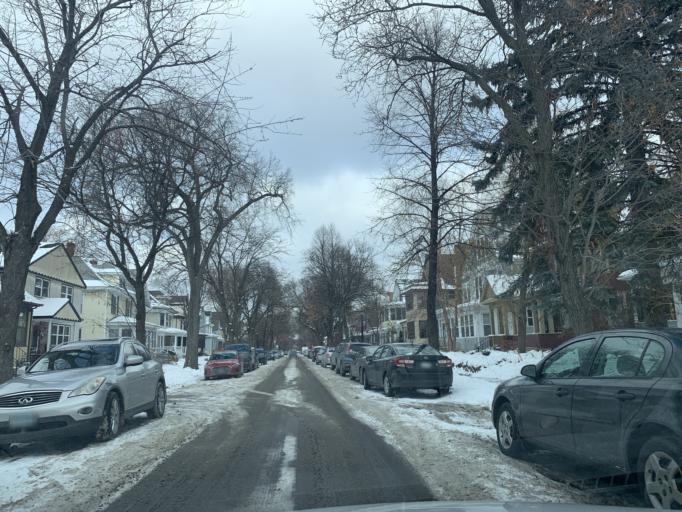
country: US
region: Minnesota
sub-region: Hennepin County
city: Minneapolis
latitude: 44.9523
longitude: -93.2957
